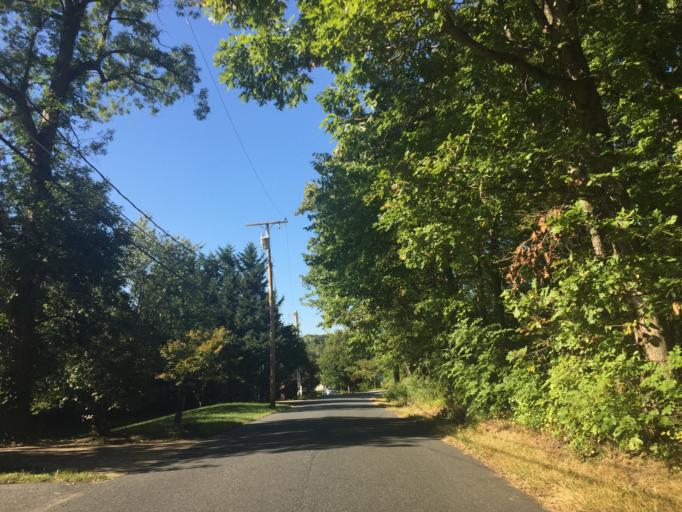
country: US
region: Maryland
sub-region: Baltimore County
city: Rossville
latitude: 39.3437
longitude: -76.4810
